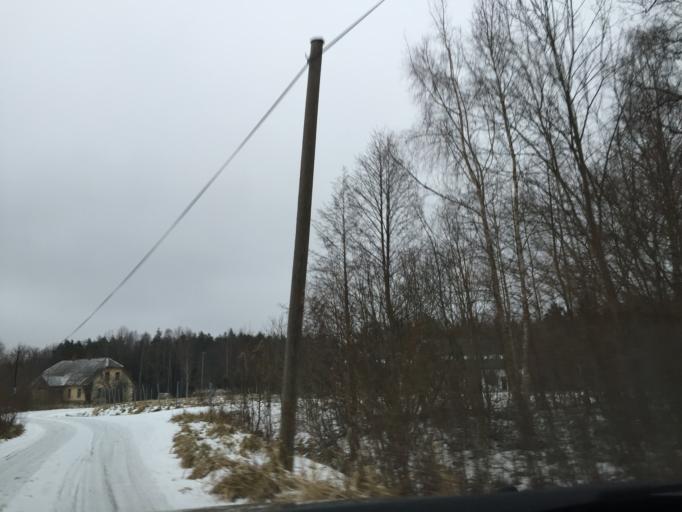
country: LV
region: Salacgrivas
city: Salacgriva
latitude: 57.5153
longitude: 24.3812
